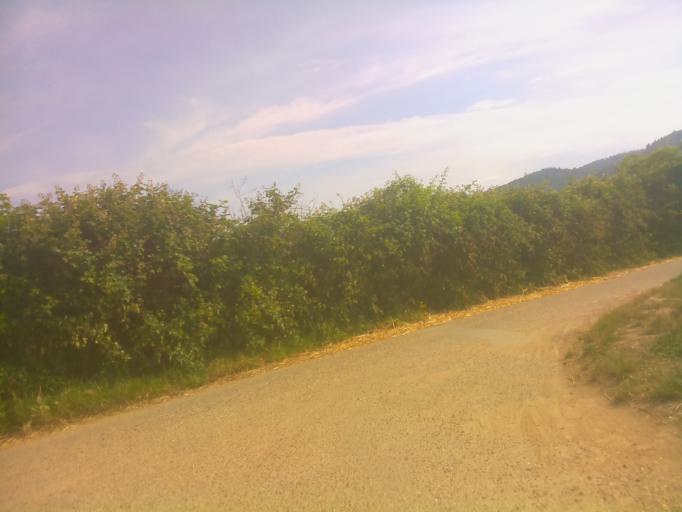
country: DE
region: Baden-Wuerttemberg
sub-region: Karlsruhe Region
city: Schriesheim
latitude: 49.5063
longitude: 8.6497
